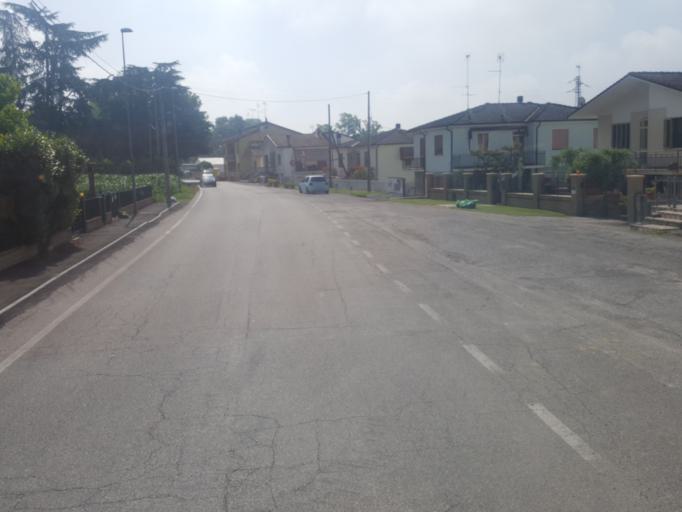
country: IT
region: Veneto
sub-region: Provincia di Rovigo
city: Canaro
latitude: 44.9360
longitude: 11.6723
